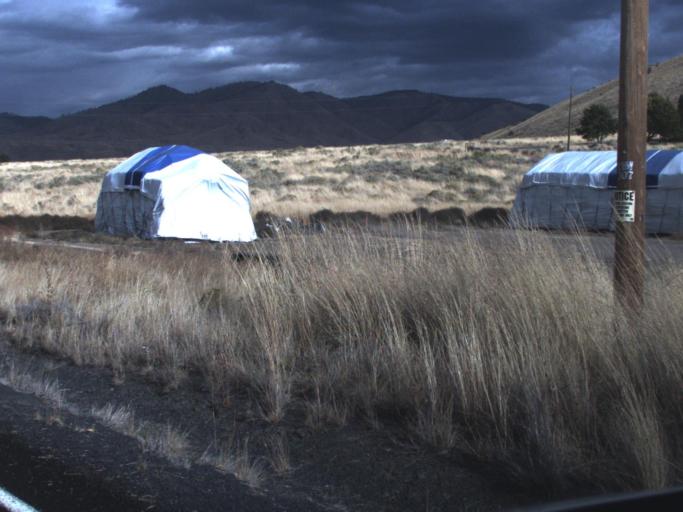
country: US
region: Washington
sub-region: Okanogan County
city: Coulee Dam
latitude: 47.9208
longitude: -118.6894
